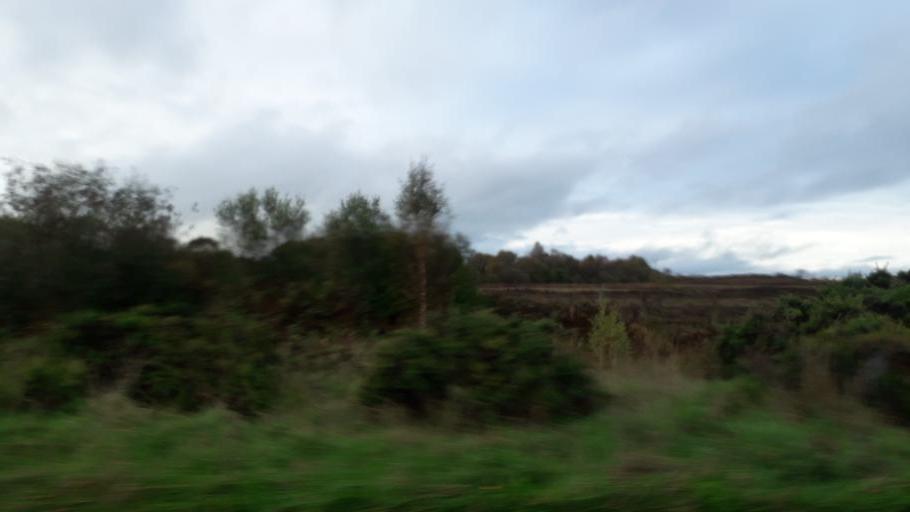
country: IE
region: Leinster
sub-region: An Longfort
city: Lanesborough
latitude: 53.7614
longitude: -7.9984
